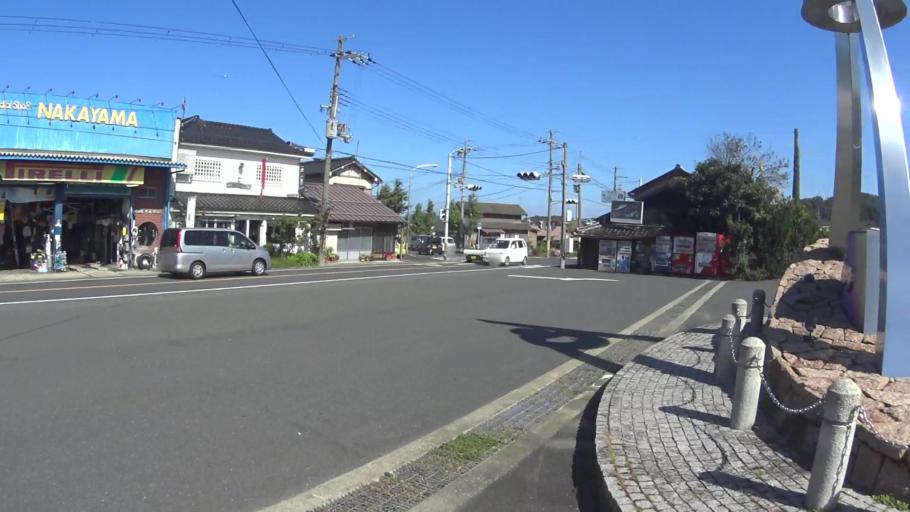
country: JP
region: Kyoto
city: Miyazu
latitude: 35.6674
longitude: 135.0249
